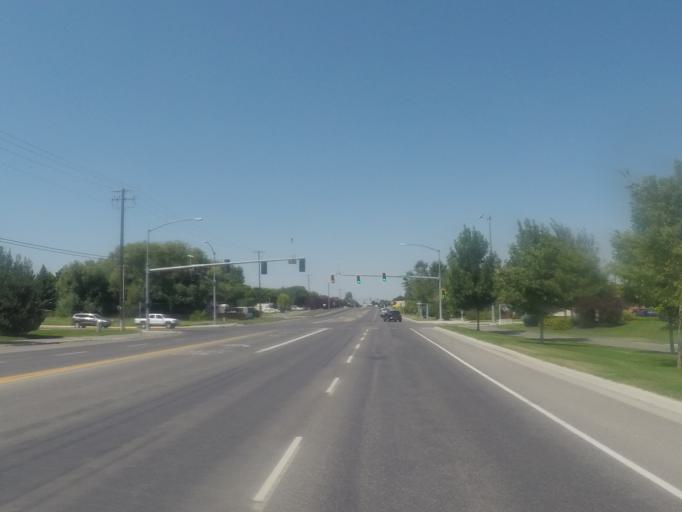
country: US
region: Montana
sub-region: Gallatin County
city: Bozeman
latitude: 45.6931
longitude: -111.0560
